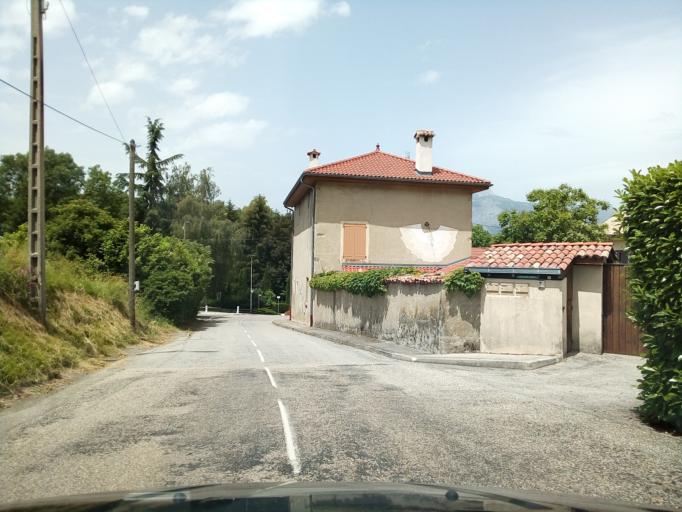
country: FR
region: Rhone-Alpes
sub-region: Departement de l'Isere
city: Gieres
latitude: 45.1706
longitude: 5.7821
